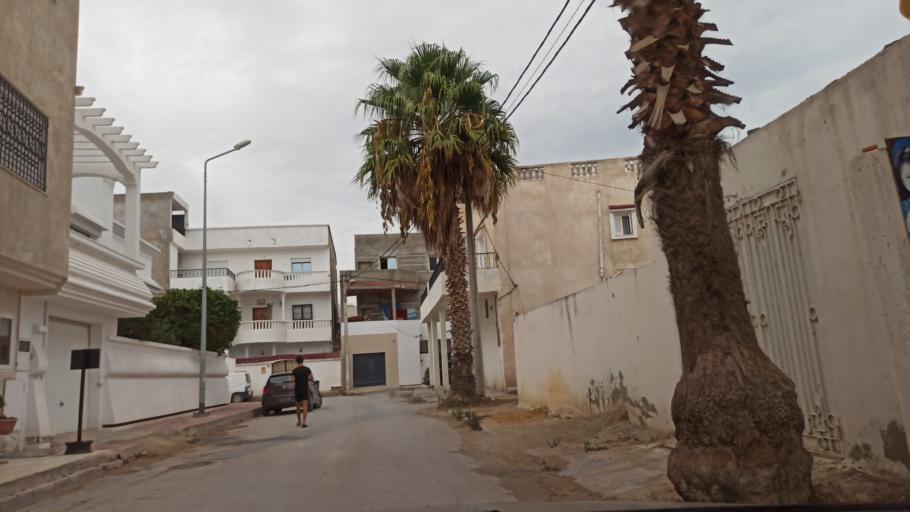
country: TN
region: Tunis
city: La Goulette
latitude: 36.8536
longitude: 10.2672
